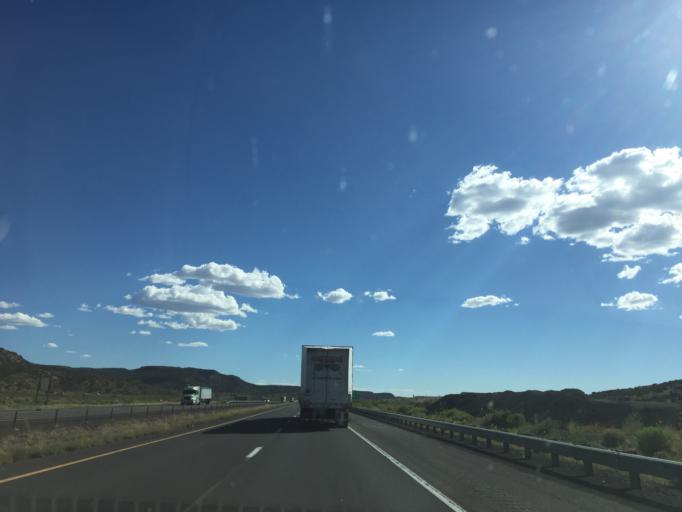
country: US
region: New Mexico
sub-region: McKinley County
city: Gallup
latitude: 35.4538
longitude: -108.9499
